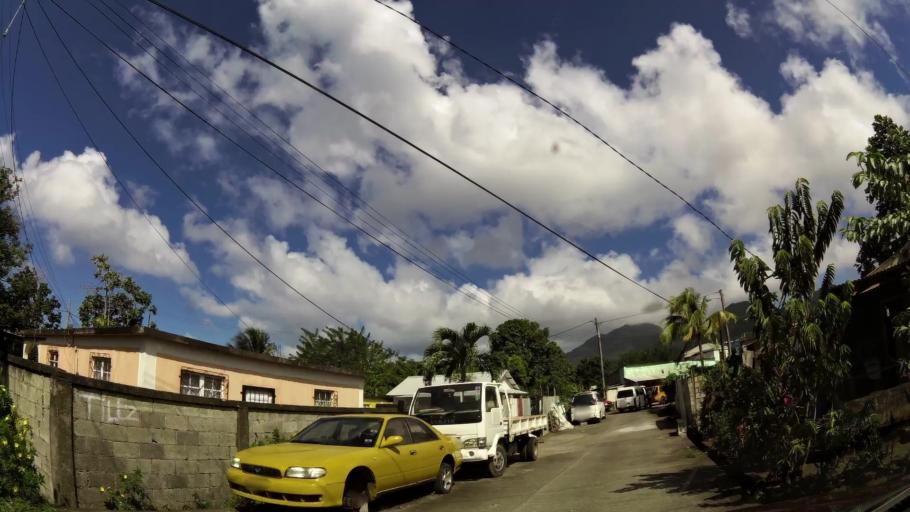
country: DM
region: Saint John
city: Portsmouth
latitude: 15.5672
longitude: -61.4564
